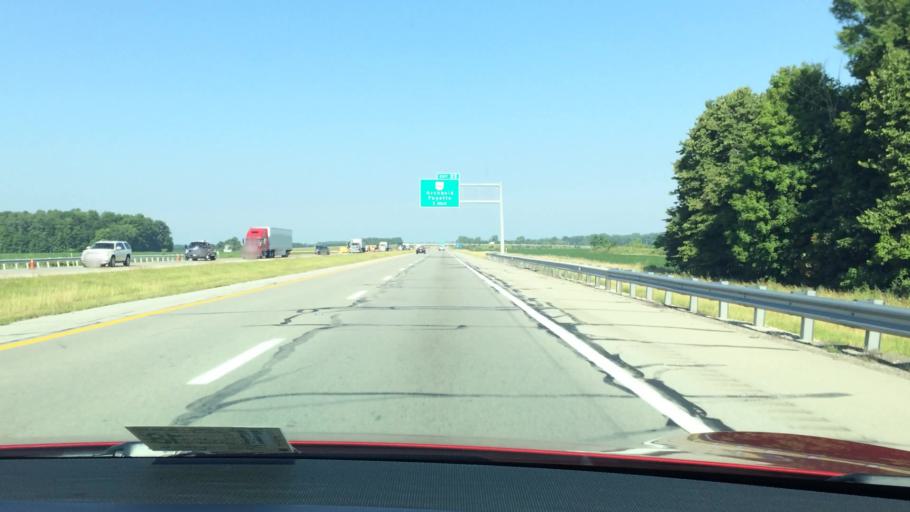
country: US
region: Ohio
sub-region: Fulton County
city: Burlington
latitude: 41.5908
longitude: -84.2939
